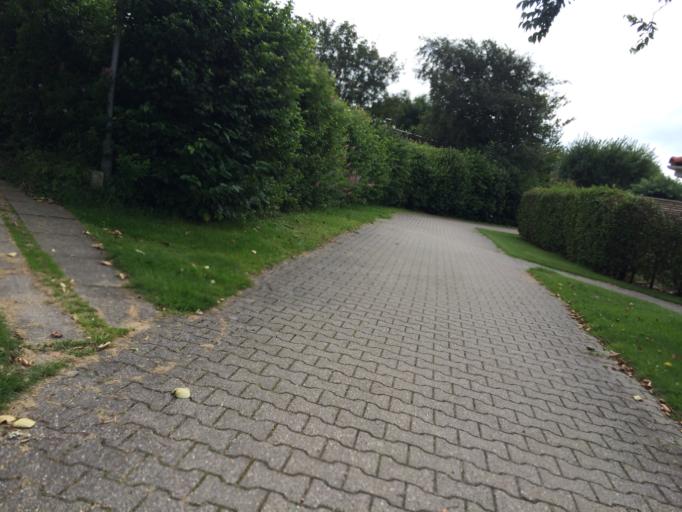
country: DK
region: Central Jutland
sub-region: Holstebro Kommune
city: Ulfborg
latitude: 56.2740
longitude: 8.3085
